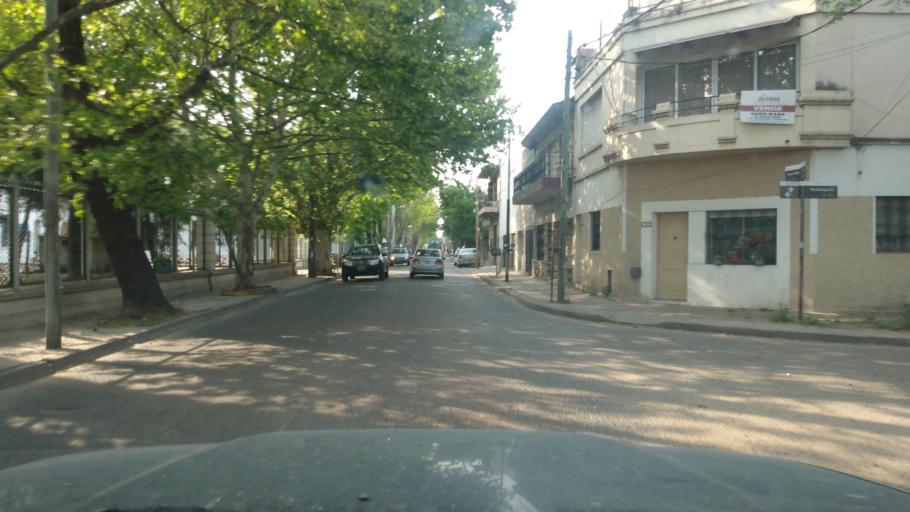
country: AR
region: Buenos Aires
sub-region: Partido de Moron
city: Moron
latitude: -34.6518
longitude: -58.6033
